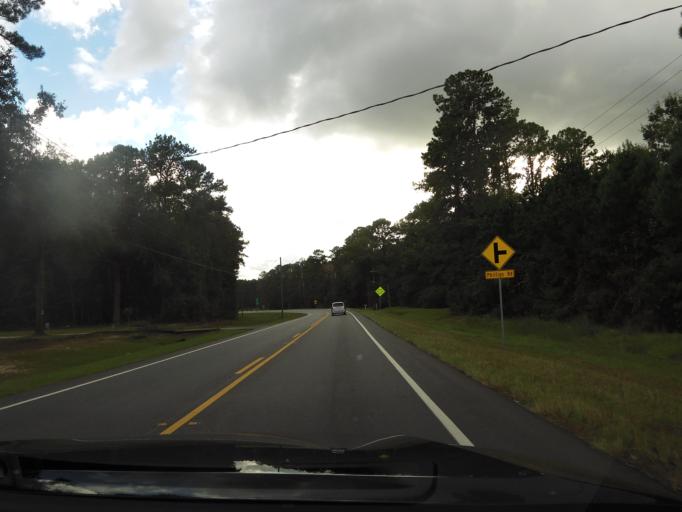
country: US
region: Georgia
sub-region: Liberty County
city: Midway
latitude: 31.8288
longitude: -81.4273
